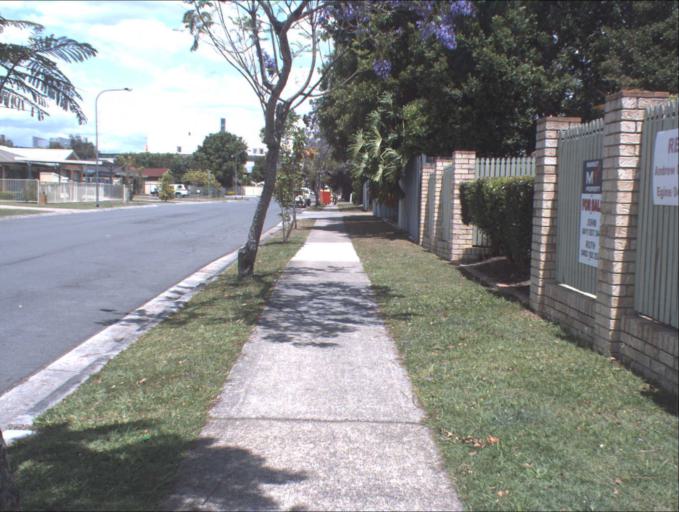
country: AU
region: Queensland
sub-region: Logan
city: Slacks Creek
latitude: -27.6667
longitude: 153.1408
